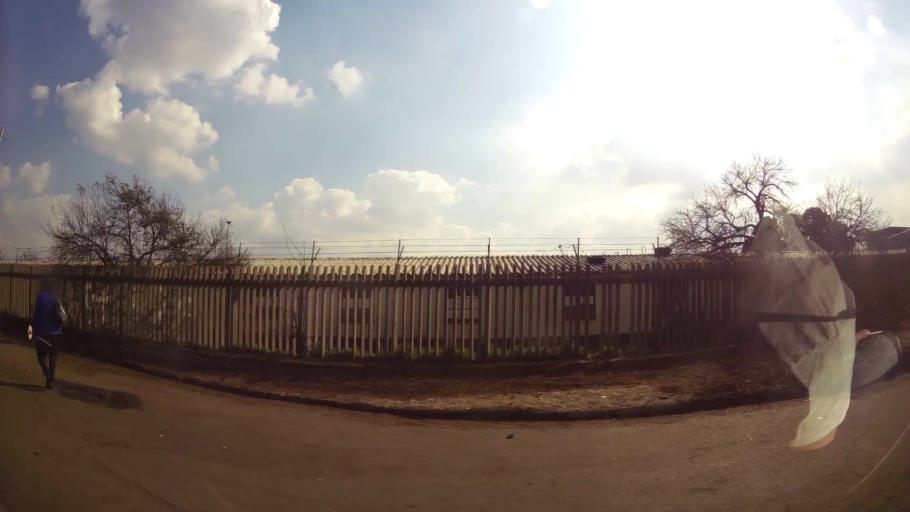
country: ZA
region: Gauteng
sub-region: Ekurhuleni Metropolitan Municipality
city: Germiston
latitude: -26.3325
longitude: 28.1429
